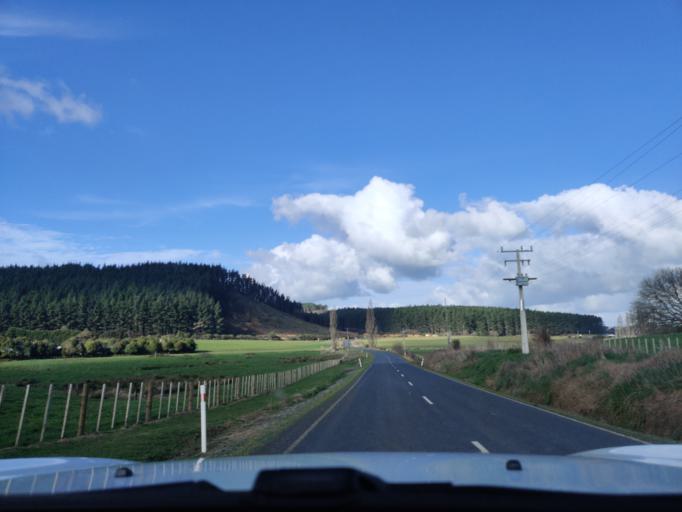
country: NZ
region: Waikato
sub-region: Waikato District
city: Te Kauwhata
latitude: -37.2912
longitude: 175.2226
